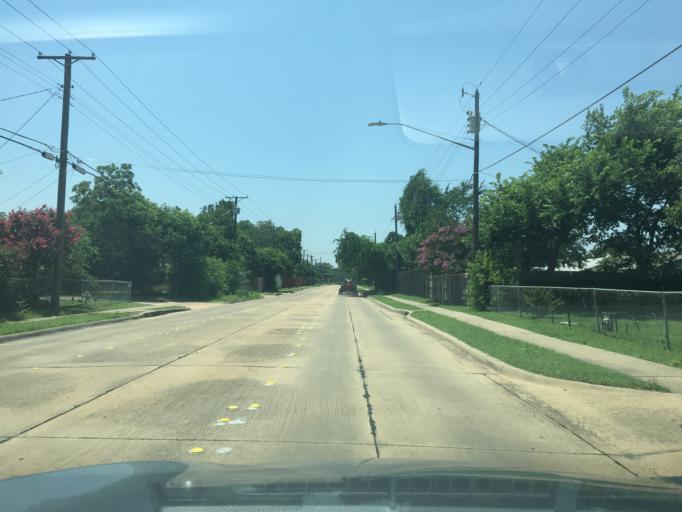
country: US
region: Texas
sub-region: Dallas County
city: Richardson
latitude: 32.9240
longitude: -96.6967
